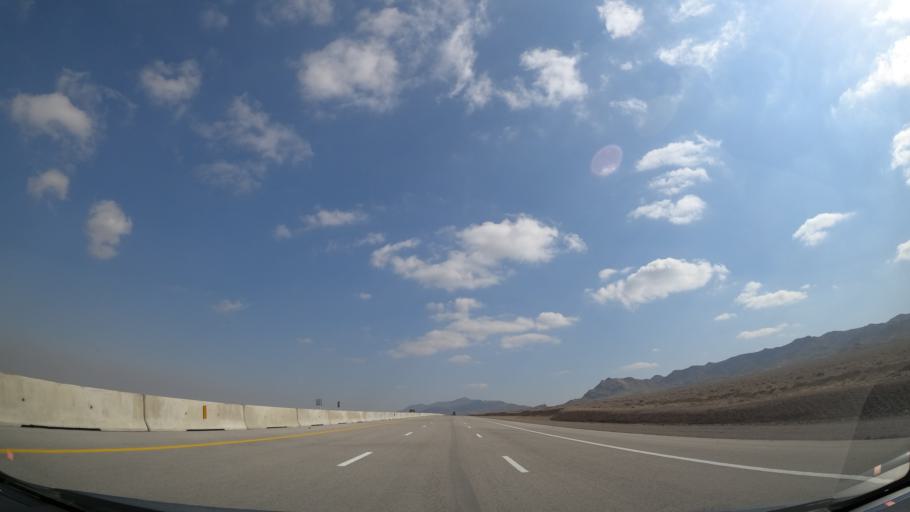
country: IR
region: Alborz
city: Eshtehard
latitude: 35.7110
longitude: 50.5947
